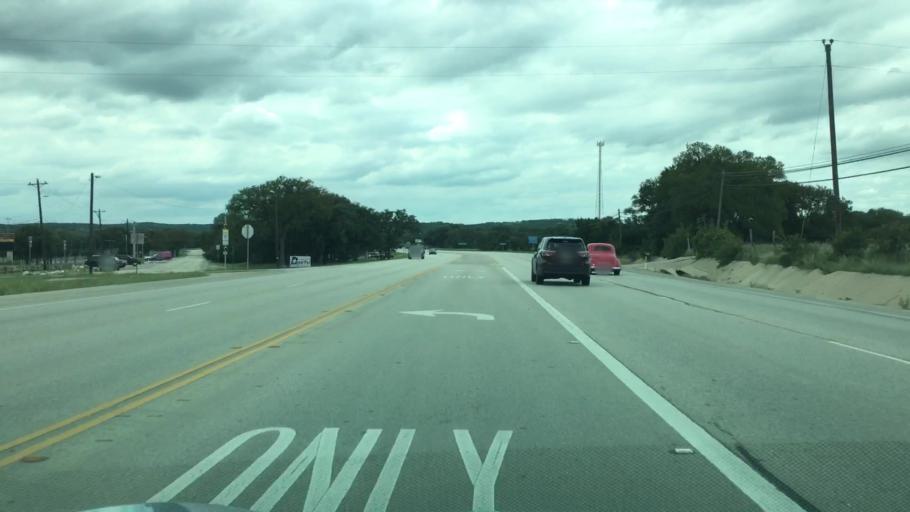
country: US
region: Texas
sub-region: Hays County
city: Dripping Springs
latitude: 30.2028
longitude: -98.1133
